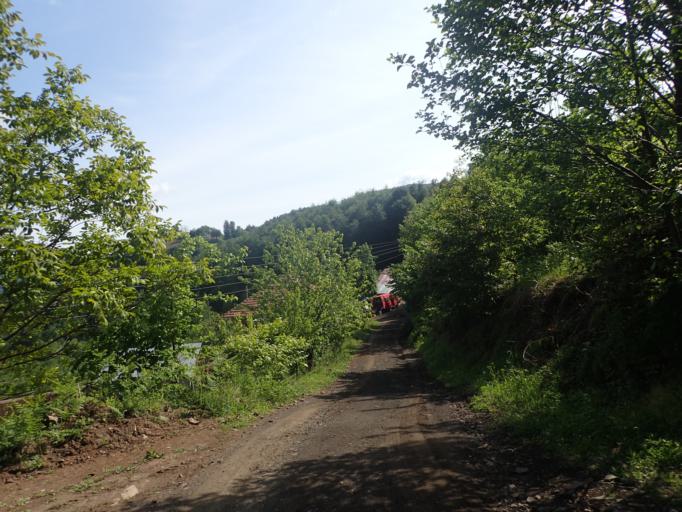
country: TR
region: Samsun
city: Salipazari
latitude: 40.9171
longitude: 36.8891
